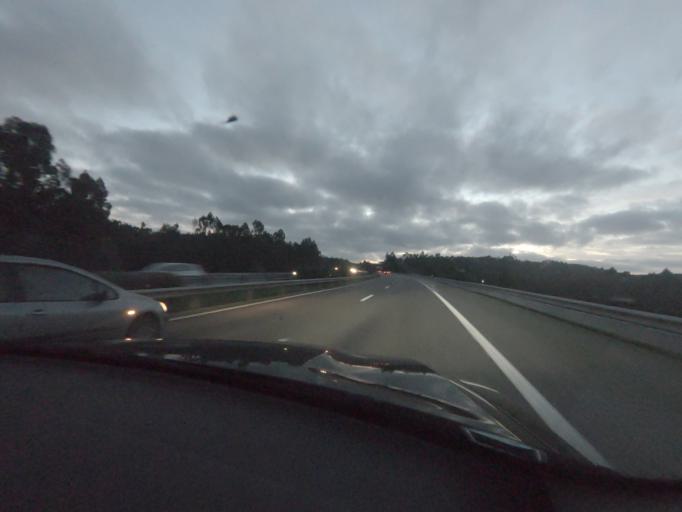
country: PT
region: Leiria
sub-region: Pombal
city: Pombal
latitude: 39.9685
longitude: -8.6555
